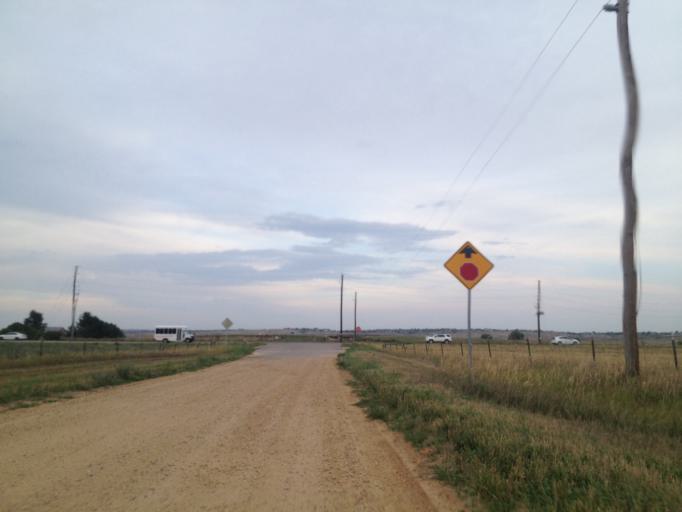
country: US
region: Colorado
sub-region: Boulder County
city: Louisville
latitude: 39.9524
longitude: -105.1295
